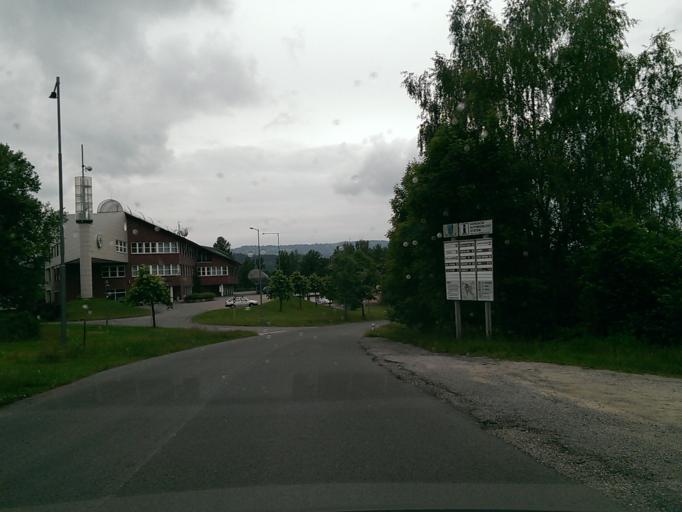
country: CZ
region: Liberecky
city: Semily
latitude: 50.6105
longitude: 15.3407
